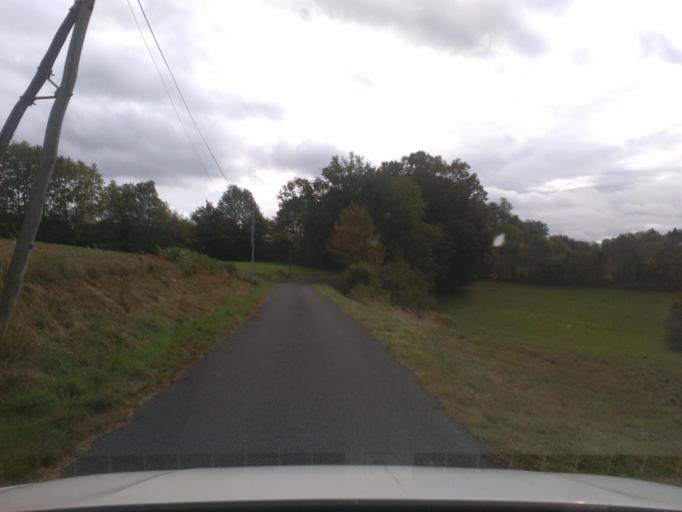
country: FR
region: Lorraine
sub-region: Departement des Vosges
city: Senones
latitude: 48.3597
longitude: 7.0071
